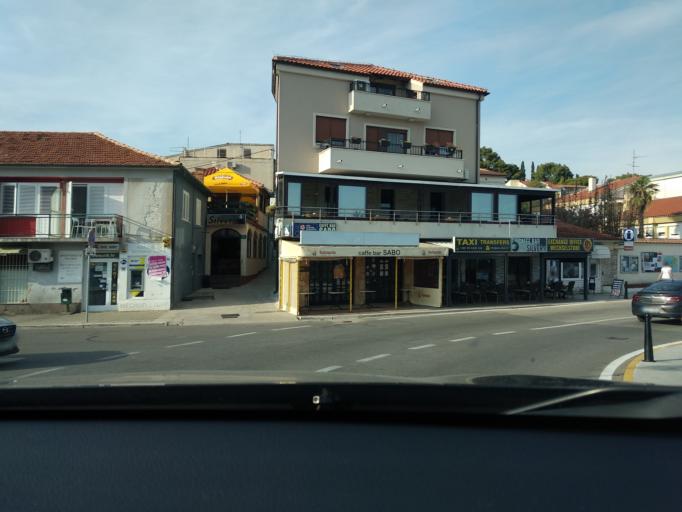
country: HR
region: Sibensko-Kniniska
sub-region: Grad Sibenik
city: Tisno
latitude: 43.8020
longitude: 15.6573
